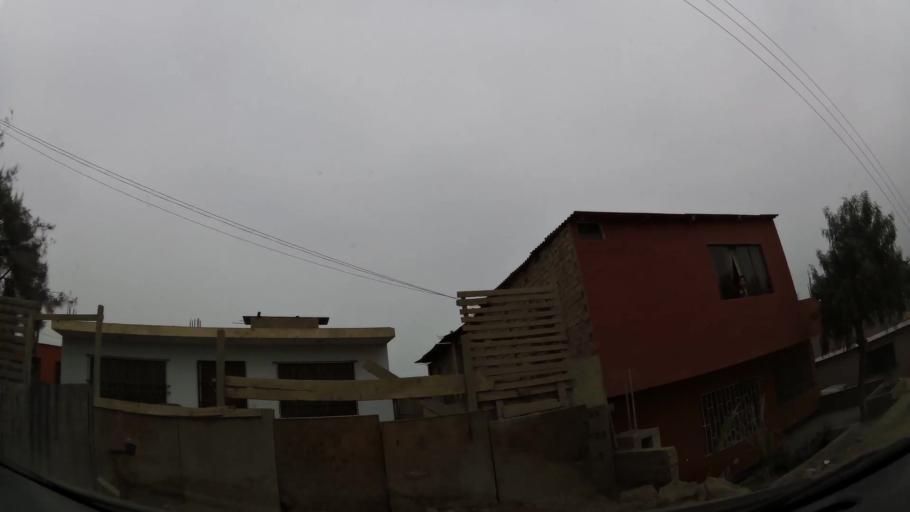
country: PE
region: Lima
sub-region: Lima
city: Surco
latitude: -12.2058
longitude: -76.9800
